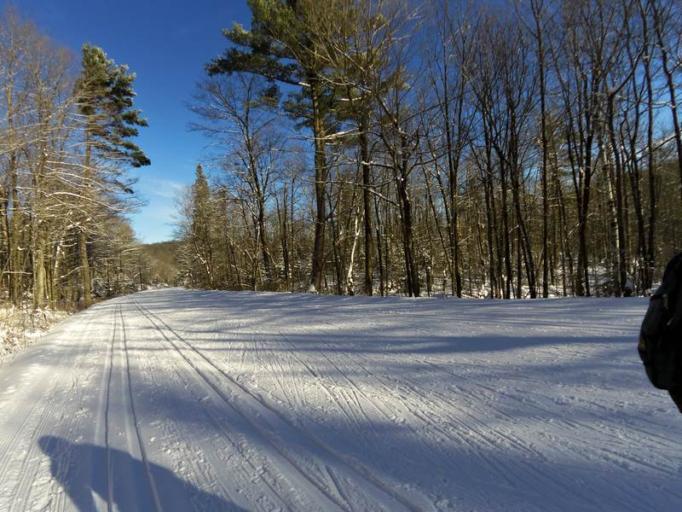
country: CA
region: Quebec
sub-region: Outaouais
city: Wakefield
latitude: 45.5077
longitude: -75.8801
